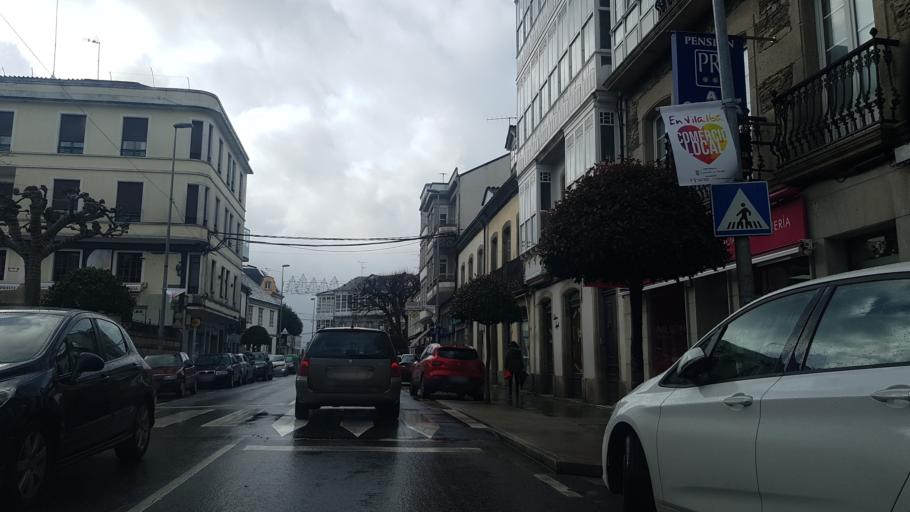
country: ES
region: Galicia
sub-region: Provincia de Lugo
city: Vilalba
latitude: 43.2984
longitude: -7.6809
